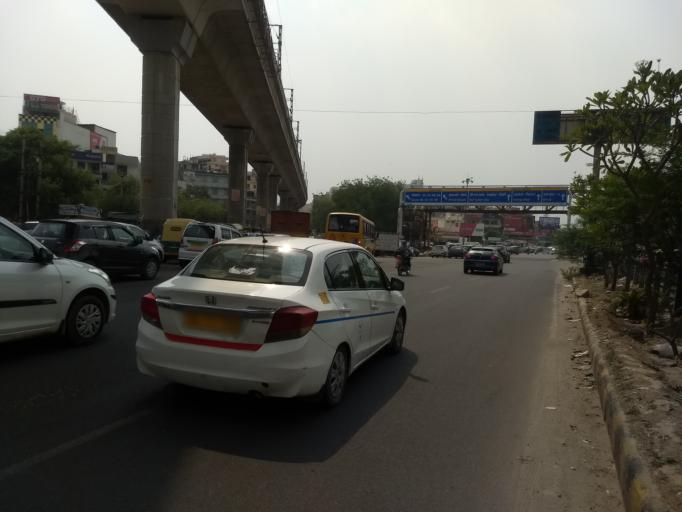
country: IN
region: Haryana
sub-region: Gurgaon
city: Gurgaon
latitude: 28.4819
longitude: 77.1003
